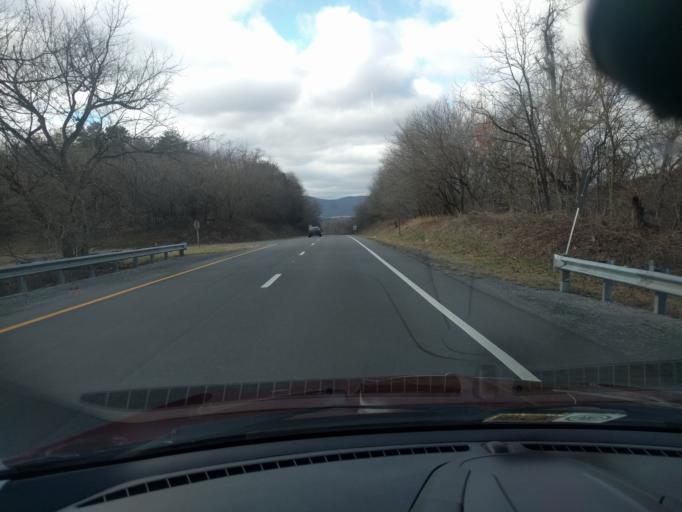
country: US
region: Virginia
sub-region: Botetourt County
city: Blue Ridge
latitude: 37.3656
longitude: -79.6898
